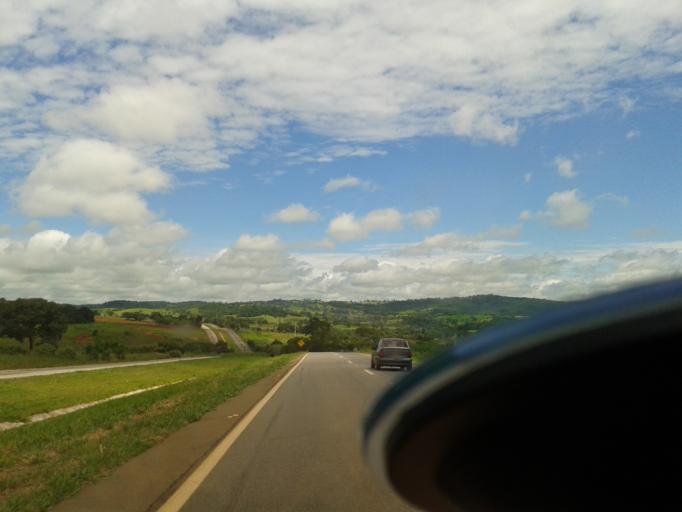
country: BR
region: Goias
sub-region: Inhumas
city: Inhumas
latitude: -16.2332
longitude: -49.5587
